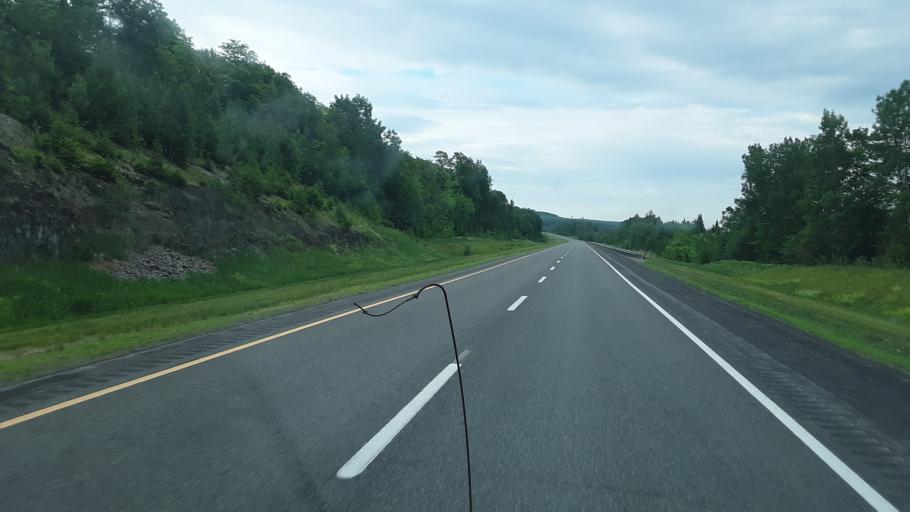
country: US
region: Maine
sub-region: Penobscot County
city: Medway
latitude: 45.7756
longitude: -68.4454
